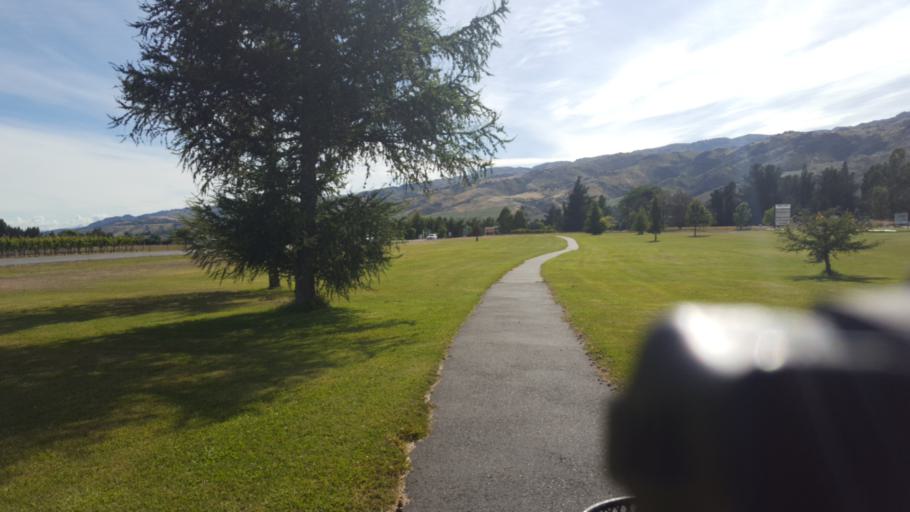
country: NZ
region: Otago
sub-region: Queenstown-Lakes District
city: Wanaka
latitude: -45.0351
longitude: 169.2010
